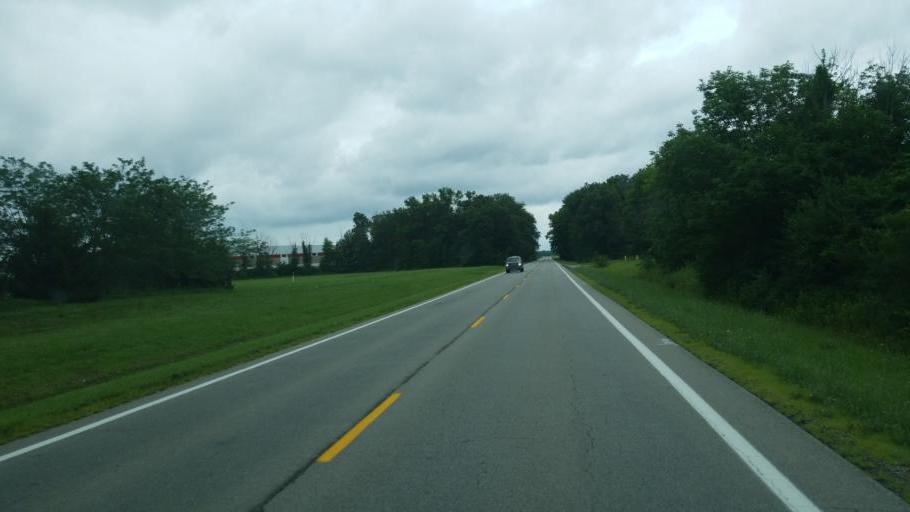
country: US
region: Ohio
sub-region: Franklin County
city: Groveport
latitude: 39.8342
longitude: -82.9172
